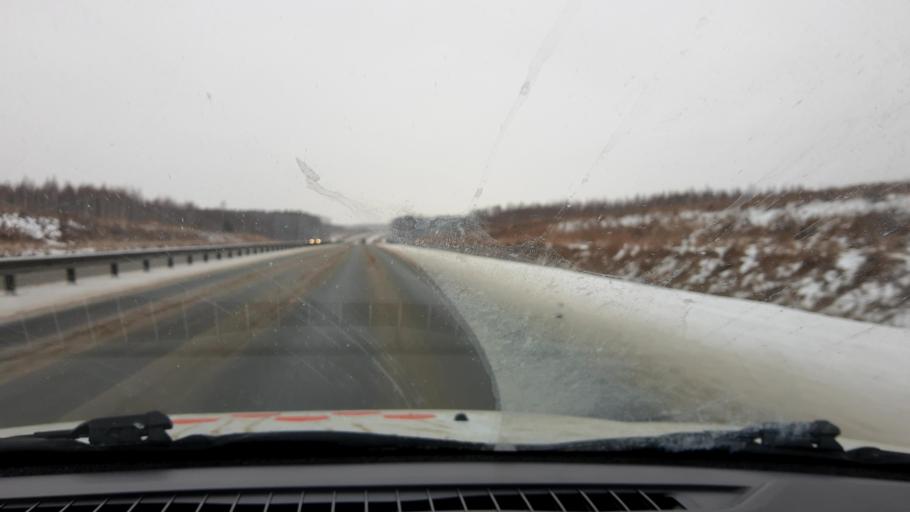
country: RU
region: Nizjnij Novgorod
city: Afonino
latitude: 56.1057
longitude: 43.9981
